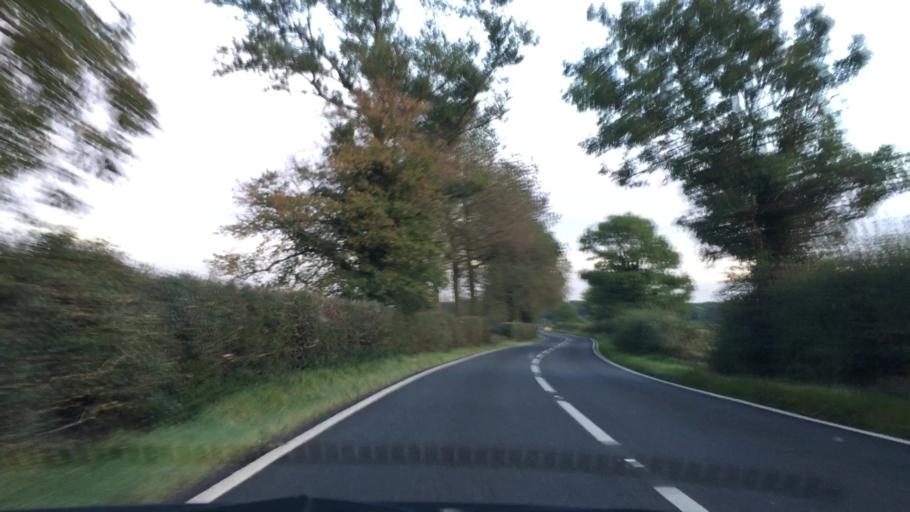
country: GB
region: England
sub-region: North East Lincolnshire
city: Wold Newton
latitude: 53.4598
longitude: -0.0926
